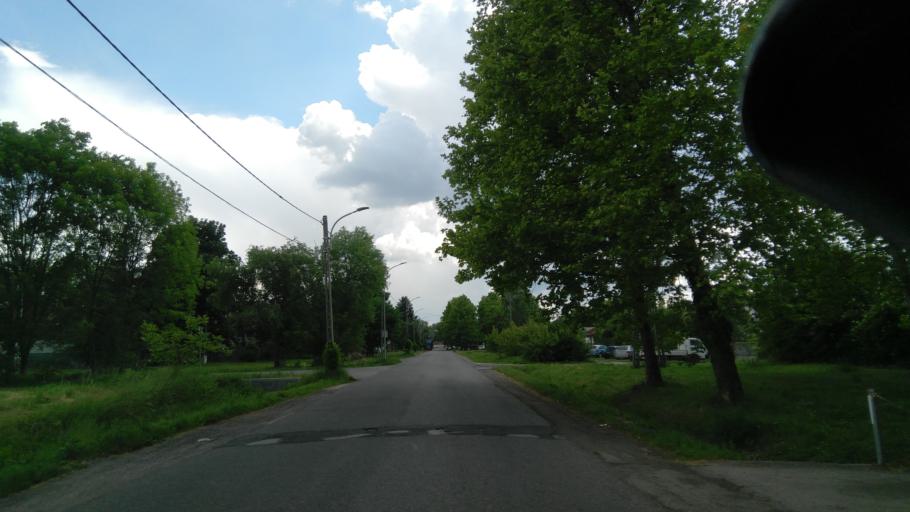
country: HU
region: Bekes
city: Gyula
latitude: 46.6613
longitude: 21.2696
